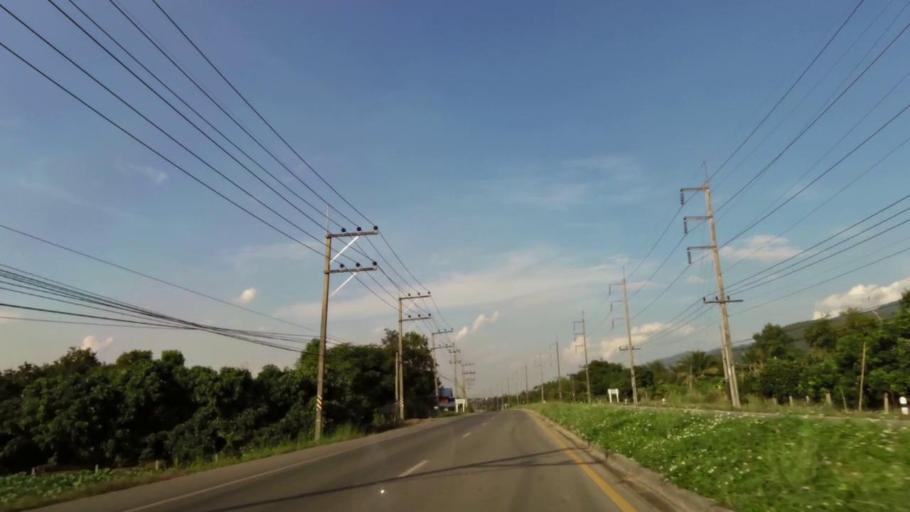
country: TH
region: Chiang Rai
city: Khun Tan
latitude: 19.8987
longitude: 100.2953
